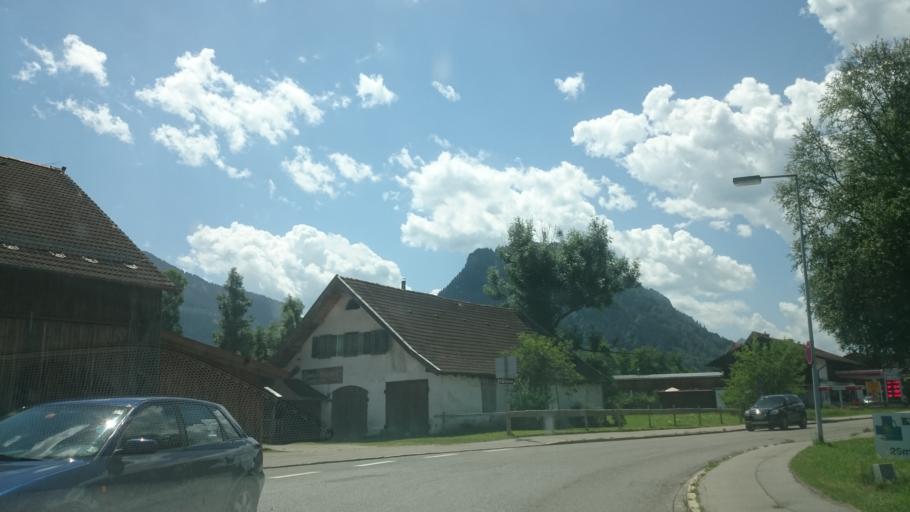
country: DE
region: Bavaria
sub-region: Swabia
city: Pfronten
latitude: 47.5839
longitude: 10.5671
